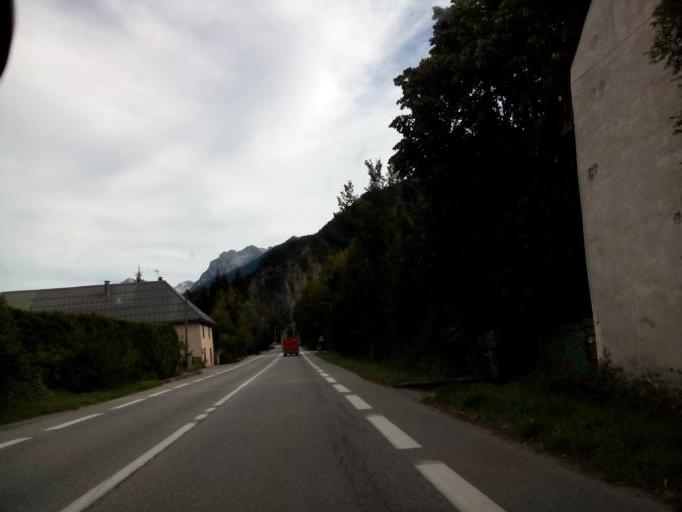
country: FR
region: Rhone-Alpes
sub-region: Departement de l'Isere
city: Huez
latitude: 45.0785
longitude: 6.0142
